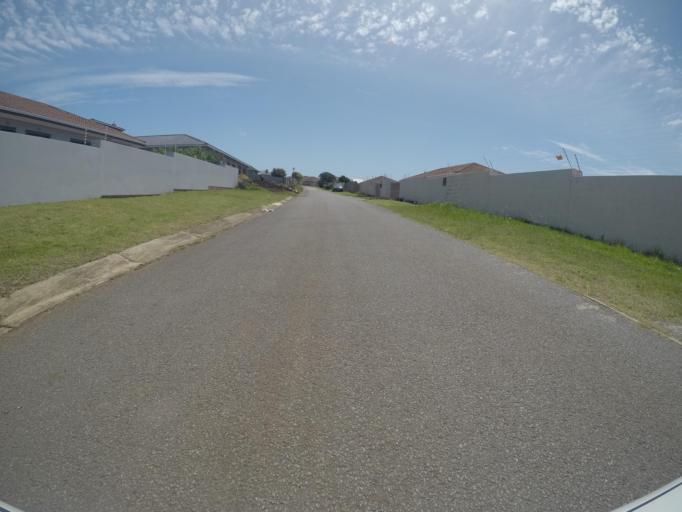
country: ZA
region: Eastern Cape
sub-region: Buffalo City Metropolitan Municipality
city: East London
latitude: -32.9428
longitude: 27.9968
